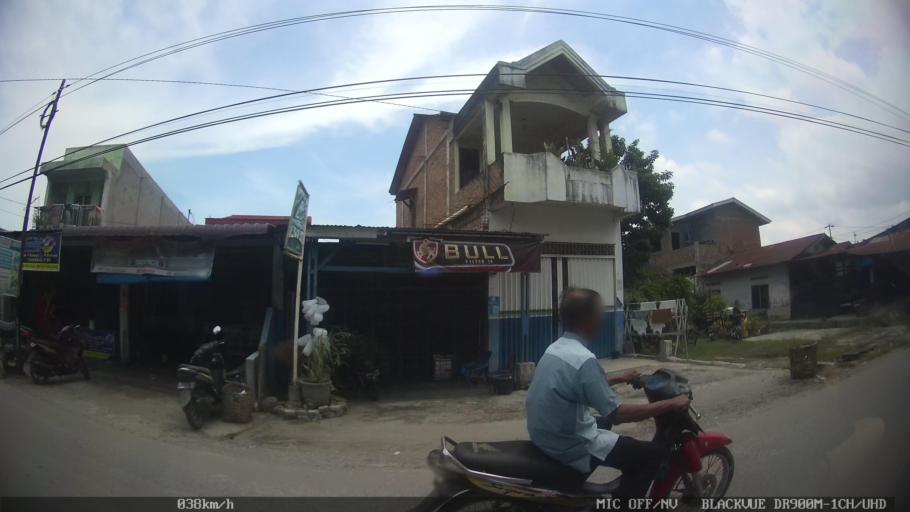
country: ID
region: North Sumatra
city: Labuhan Deli
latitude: 3.6836
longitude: 98.6896
